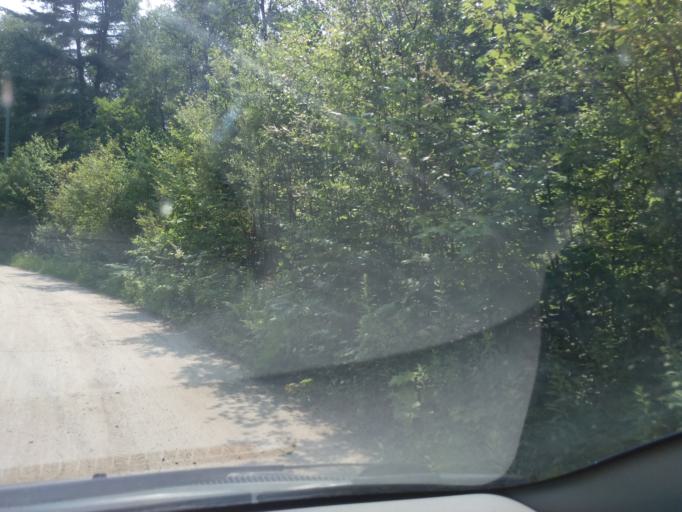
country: CA
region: Quebec
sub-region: Outaouais
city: Maniwaki
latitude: 46.2022
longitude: -76.1427
